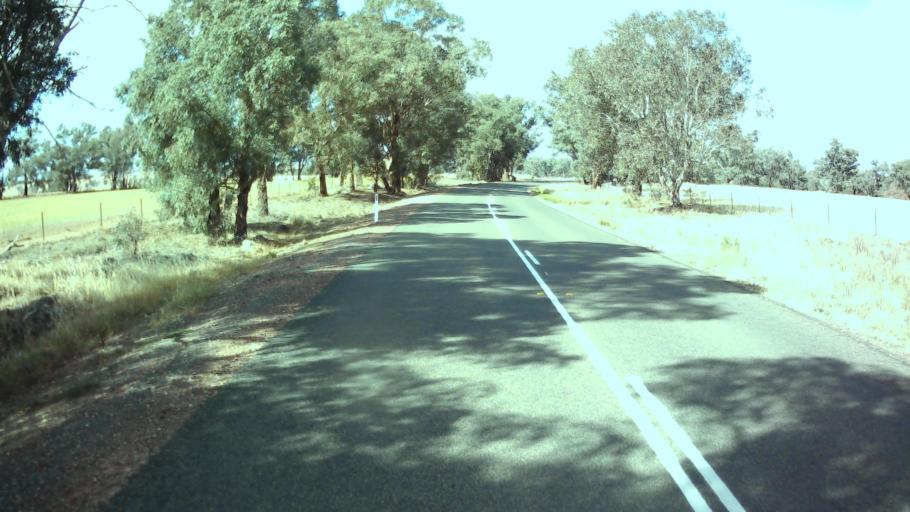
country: AU
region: New South Wales
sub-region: Weddin
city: Grenfell
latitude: -33.9844
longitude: 148.4155
